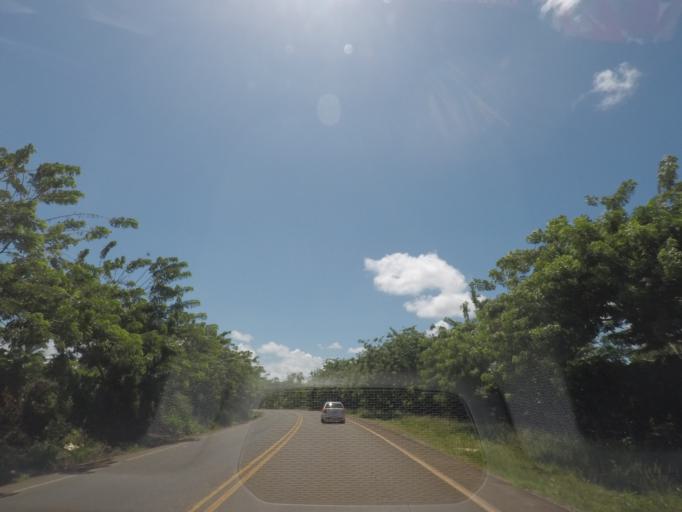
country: BR
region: Bahia
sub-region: Valenca
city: Valenca
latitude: -13.3358
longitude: -39.0624
